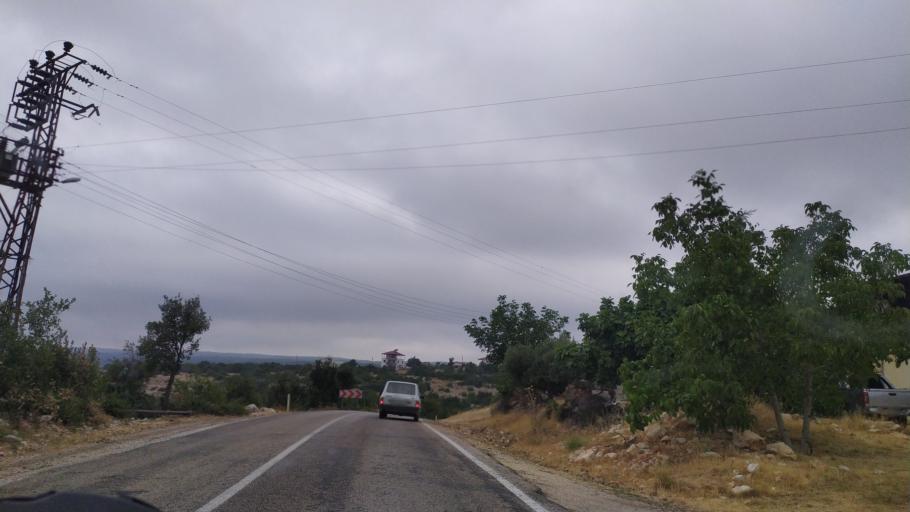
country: TR
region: Mersin
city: Silifke
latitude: 36.5501
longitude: 33.9182
